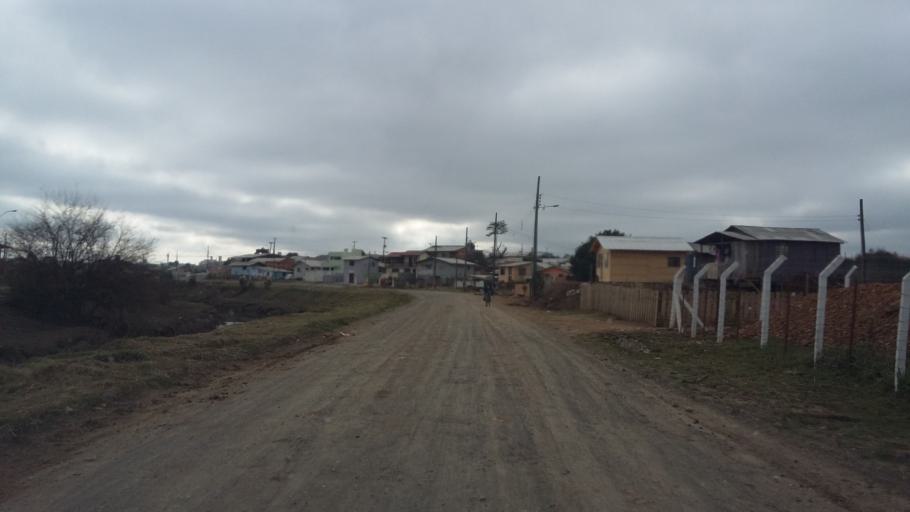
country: BR
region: Santa Catarina
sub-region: Lages
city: Lages
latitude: -27.8358
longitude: -50.3215
